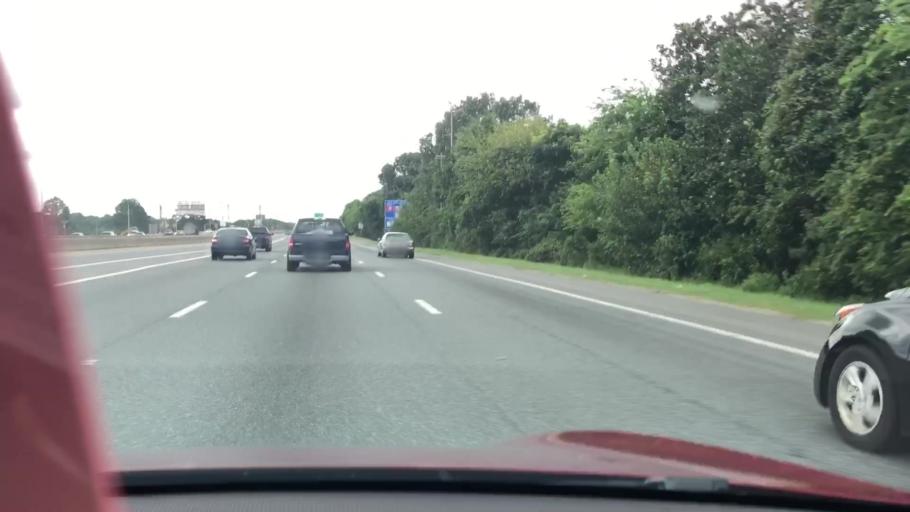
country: US
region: Virginia
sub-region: City of Chesapeake
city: Chesapeake
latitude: 36.8333
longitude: -76.1966
